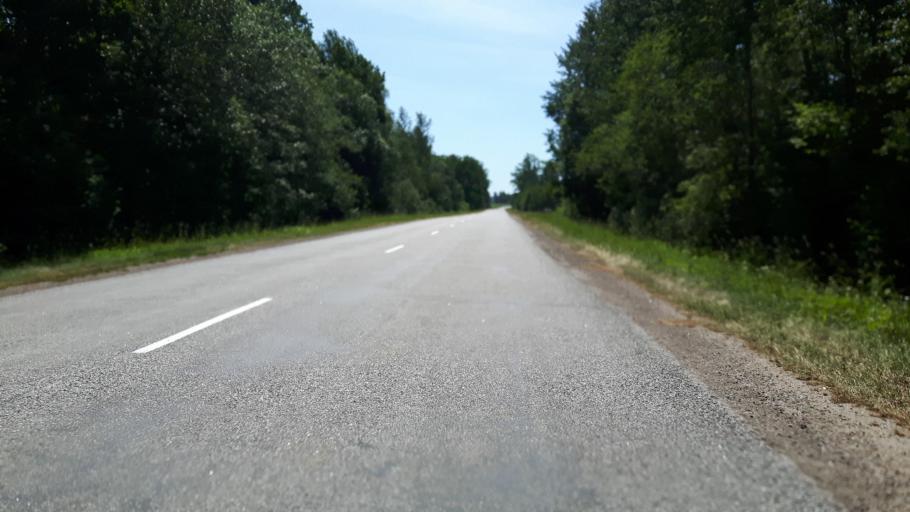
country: LV
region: Aizpute
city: Aizpute
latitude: 56.8153
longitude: 21.7214
